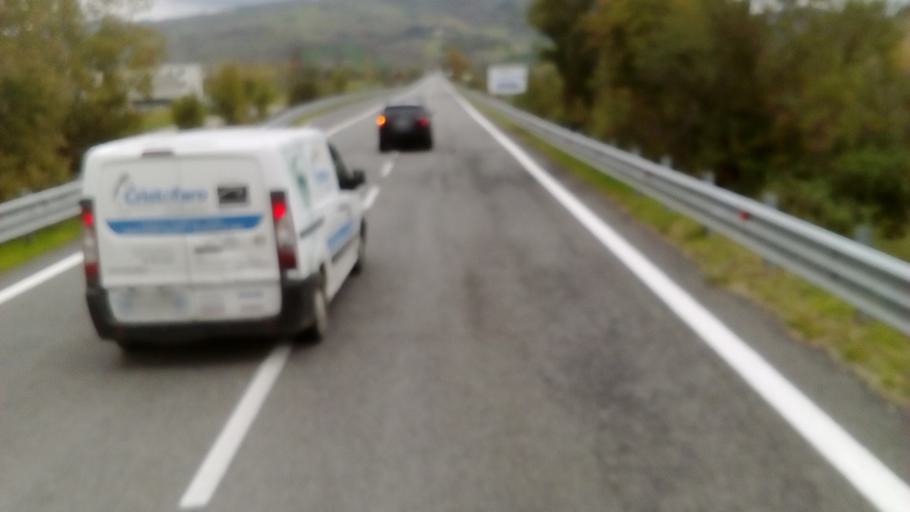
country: IT
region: Abruzzo
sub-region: Provincia di Chieti
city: San Giovanni Lipioni
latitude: 41.8085
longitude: 14.5675
